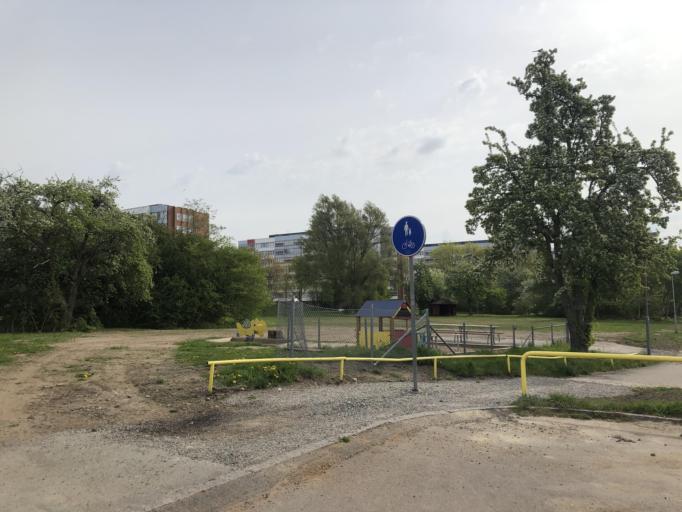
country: SE
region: Skane
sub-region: Landskrona
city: Landskrona
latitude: 55.8811
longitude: 12.8444
